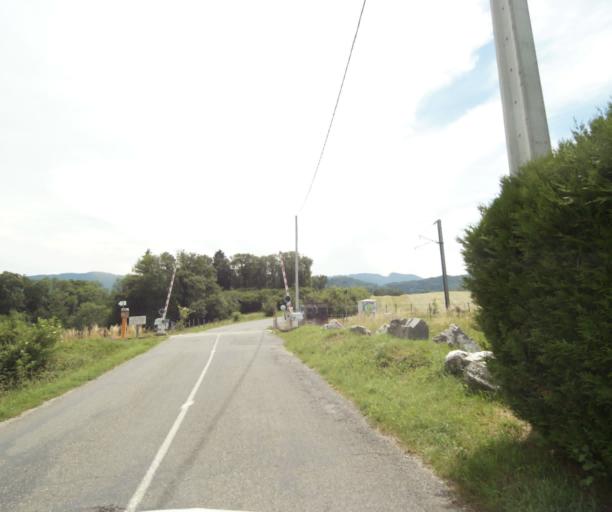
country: FR
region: Rhone-Alpes
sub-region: Departement de la Haute-Savoie
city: Allinges
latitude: 46.3496
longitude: 6.4511
